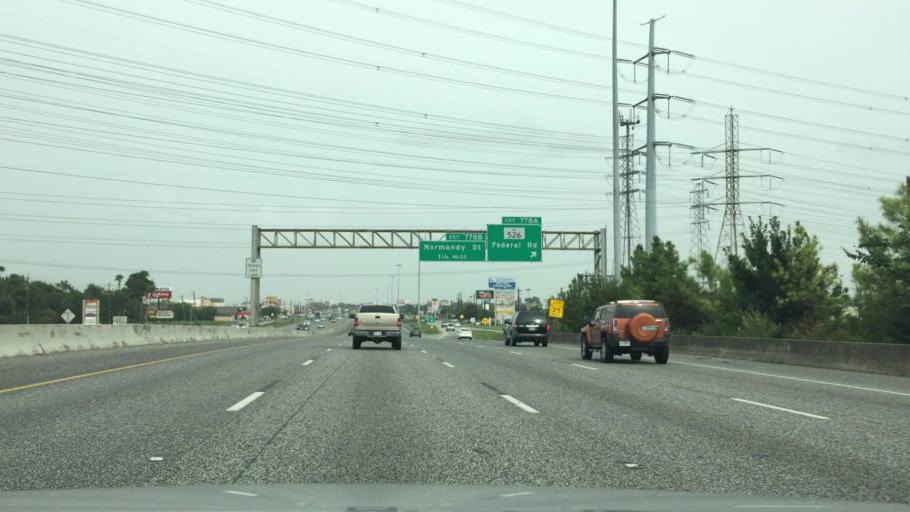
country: US
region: Texas
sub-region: Harris County
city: Jacinto City
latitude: 29.7729
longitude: -95.2321
